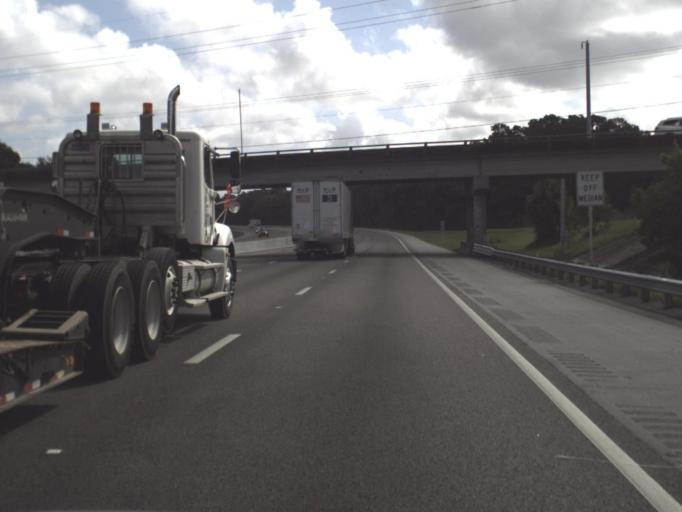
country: US
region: Florida
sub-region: Hillsborough County
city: University
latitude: 28.1071
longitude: -82.4314
